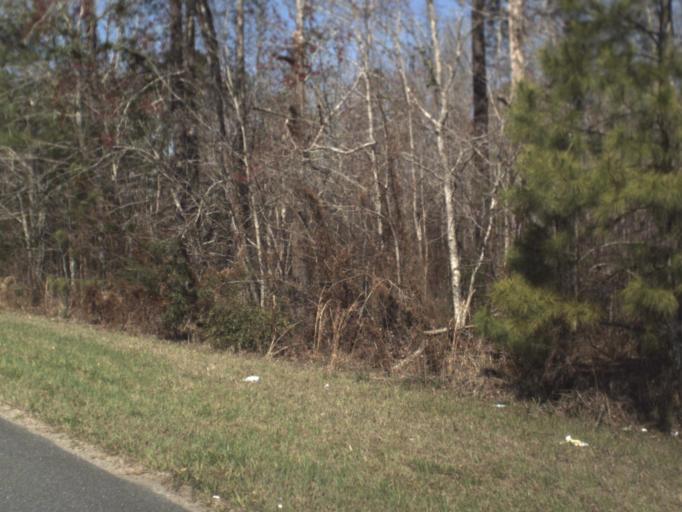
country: US
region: Florida
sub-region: Jackson County
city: Marianna
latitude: 30.7420
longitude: -85.1516
